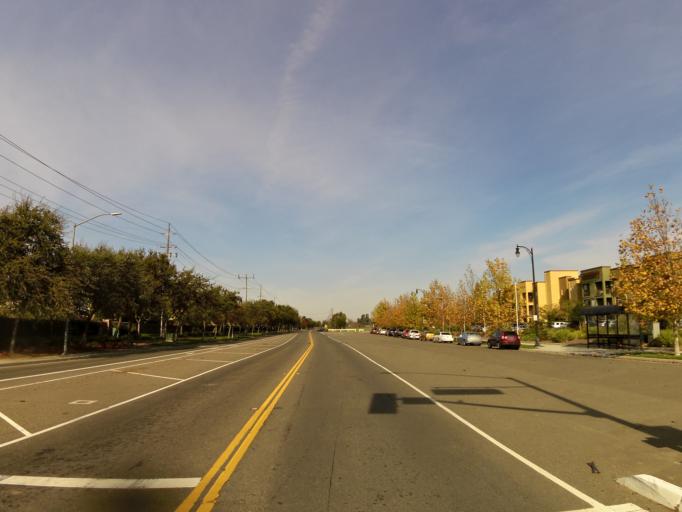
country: US
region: California
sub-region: Sacramento County
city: Laguna
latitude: 38.3796
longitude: -121.4174
